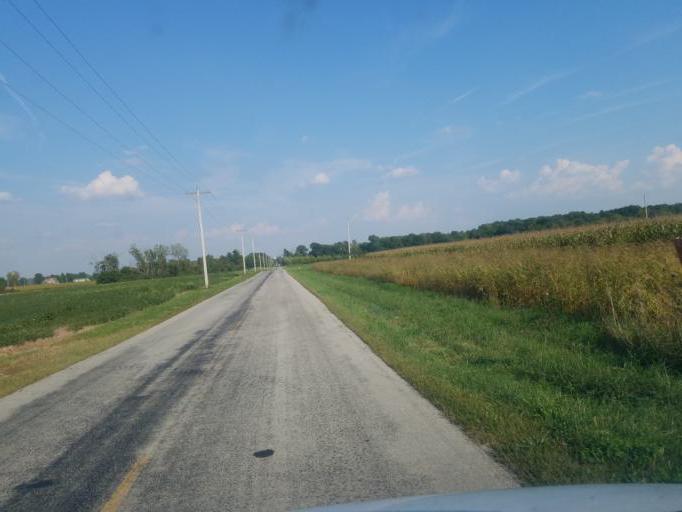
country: US
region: Ohio
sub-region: Wyandot County
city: Carey
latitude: 40.9052
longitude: -83.3905
